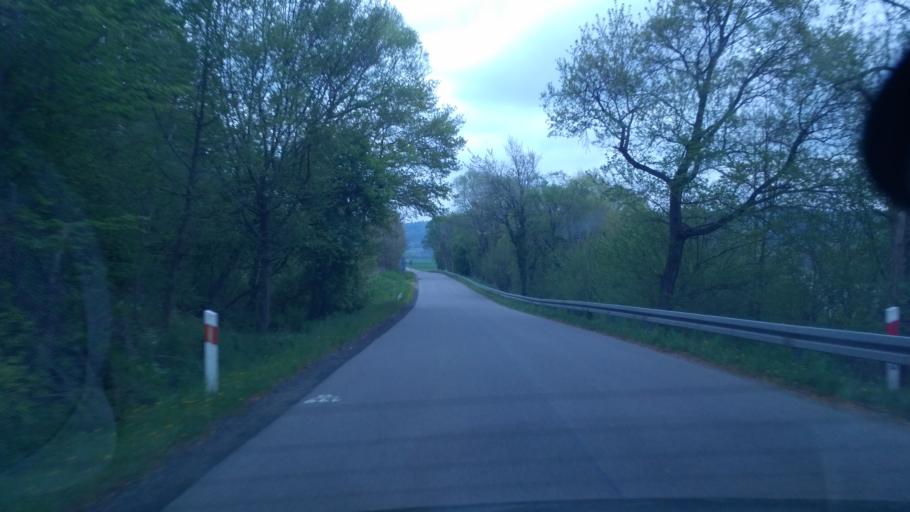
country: PL
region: Subcarpathian Voivodeship
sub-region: Powiat brzozowski
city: Nozdrzec
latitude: 49.7457
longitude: 22.2151
